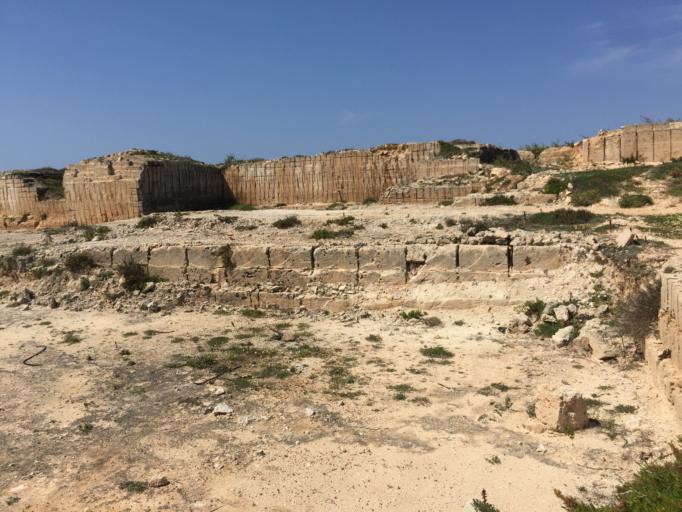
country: IT
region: Sicily
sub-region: Agrigento
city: Lampedusa
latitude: 35.4943
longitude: 12.6278
